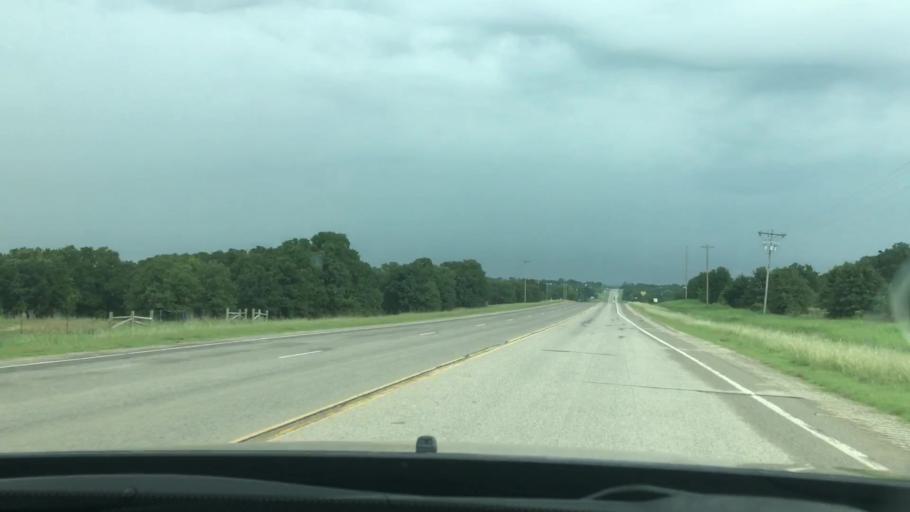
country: US
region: Oklahoma
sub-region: Carter County
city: Healdton
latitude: 34.1977
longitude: -97.4747
